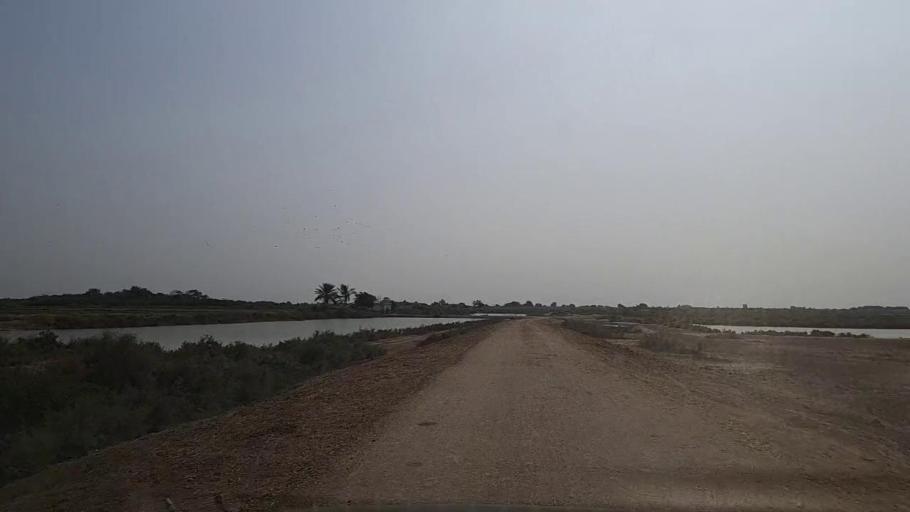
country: PK
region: Sindh
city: Thatta
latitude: 24.5709
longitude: 67.9170
